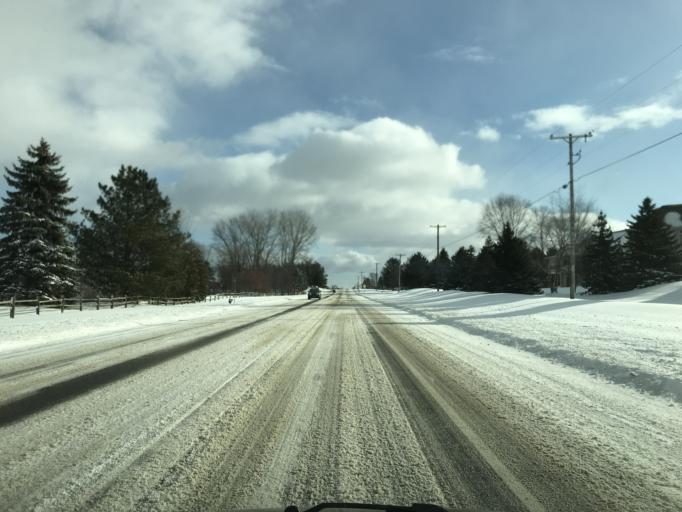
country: US
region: Michigan
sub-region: Kent County
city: Byron Center
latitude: 42.8268
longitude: -85.7301
